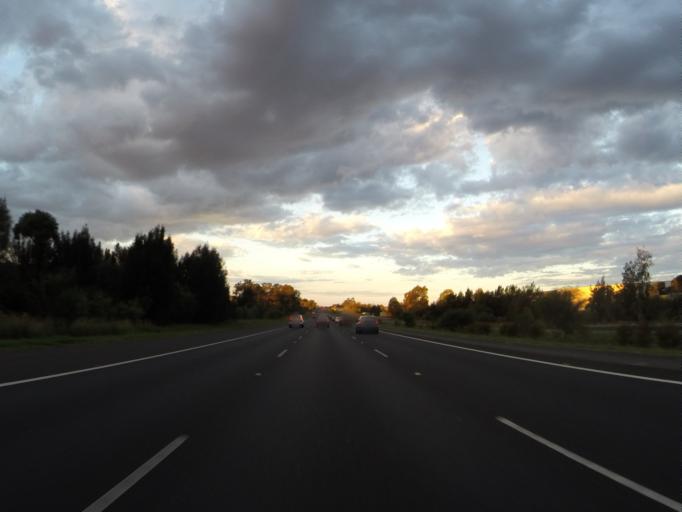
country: AU
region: New South Wales
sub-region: Campbelltown Municipality
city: Campbelltown
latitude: -34.0559
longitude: 150.7990
